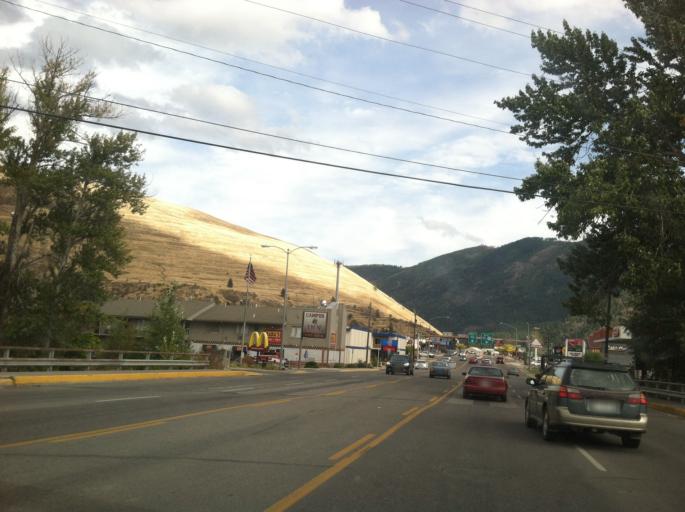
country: US
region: Montana
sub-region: Missoula County
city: Missoula
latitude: 46.8695
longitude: -113.9856
